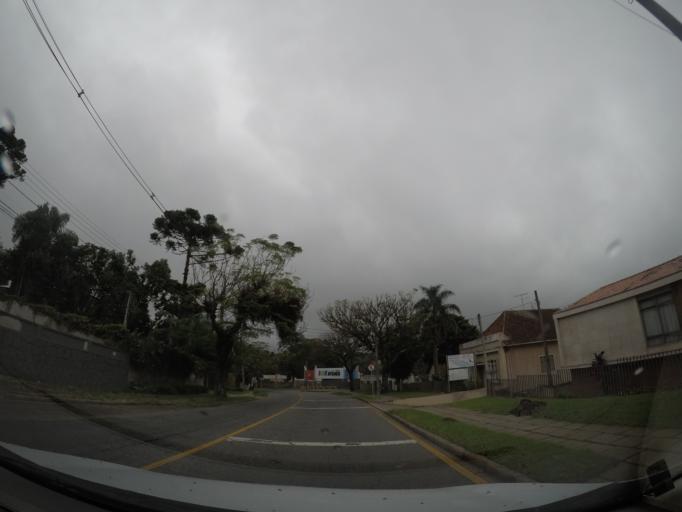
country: BR
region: Parana
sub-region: Curitiba
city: Curitiba
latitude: -25.4478
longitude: -49.3114
